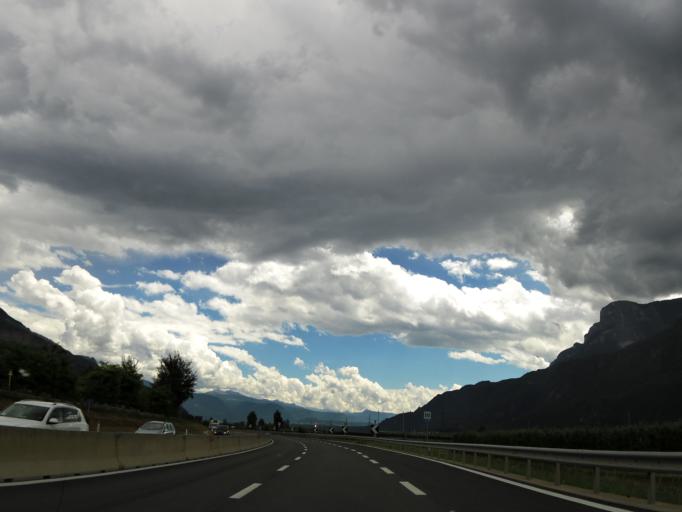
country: IT
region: Trentino-Alto Adige
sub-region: Bolzano
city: Nalles
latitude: 46.5526
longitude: 11.2186
